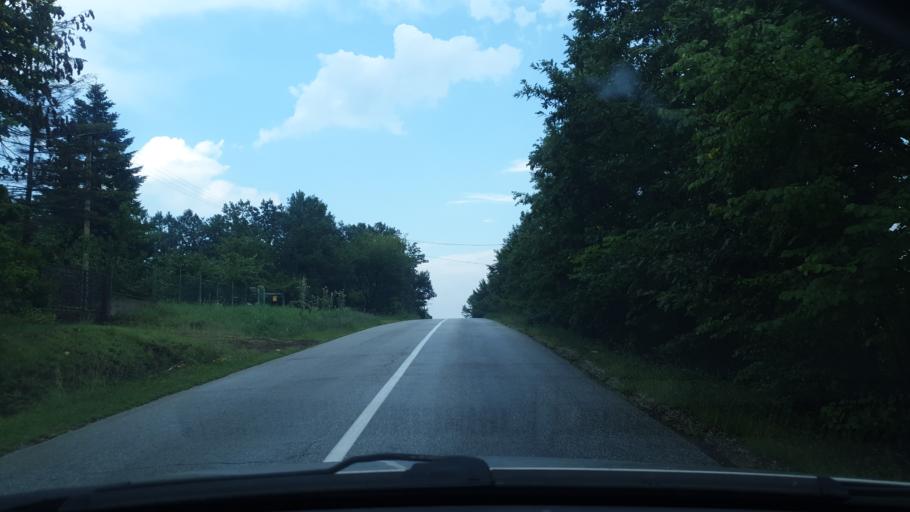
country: RS
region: Central Serbia
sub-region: Sumadijski Okrug
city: Kragujevac
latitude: 44.0437
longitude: 20.7940
